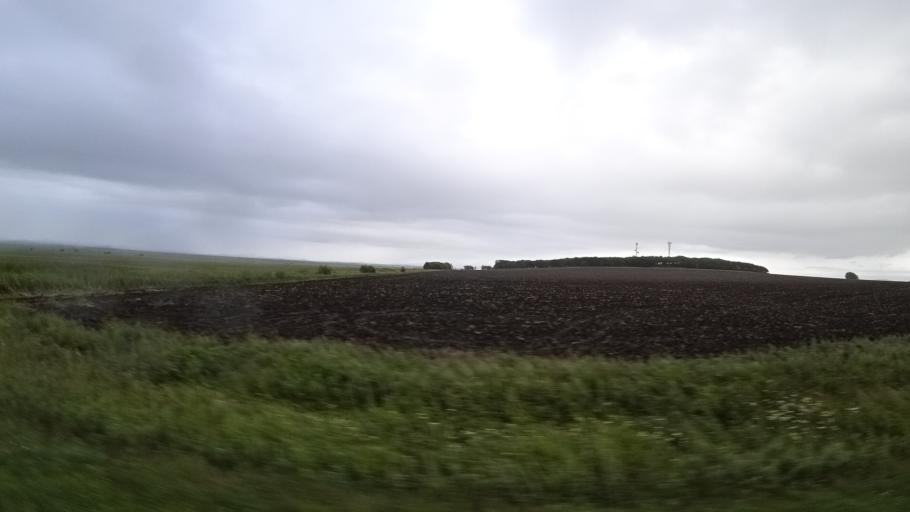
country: RU
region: Primorskiy
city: Chernigovka
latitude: 44.3723
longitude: 132.5299
